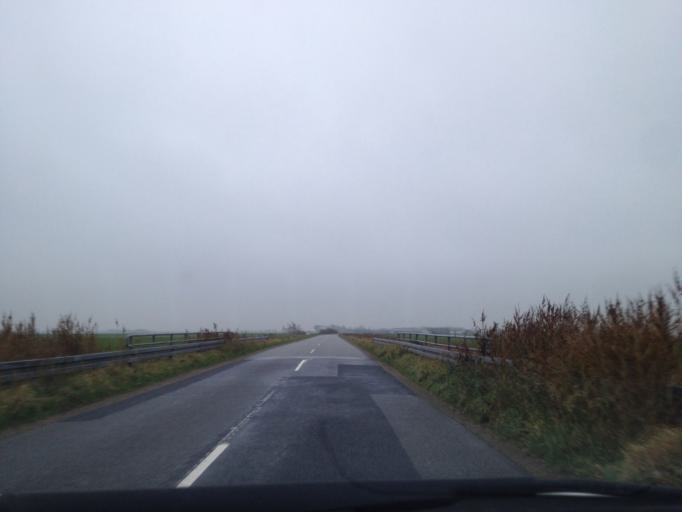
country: DK
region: South Denmark
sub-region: Tonder Kommune
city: Sherrebek
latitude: 55.1029
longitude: 8.7275
